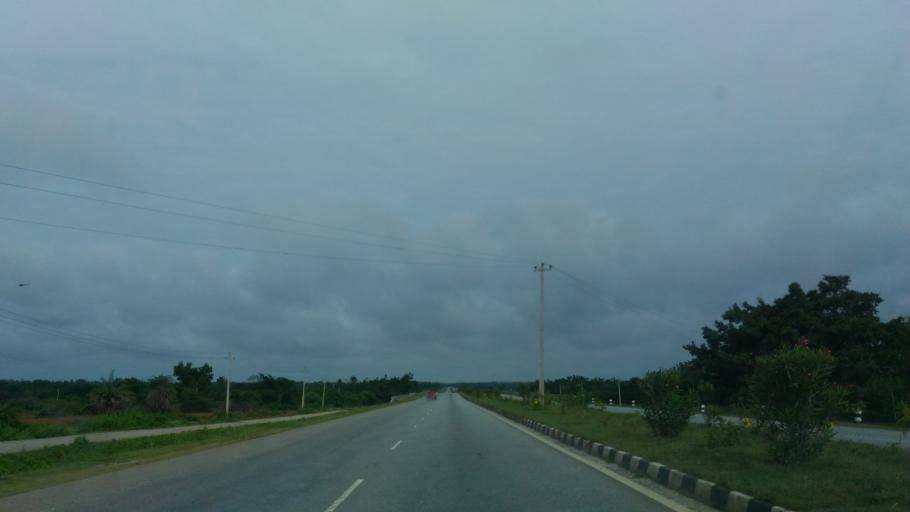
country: IN
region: Karnataka
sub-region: Tumkur
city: Kunigal
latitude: 13.0050
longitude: 77.0100
